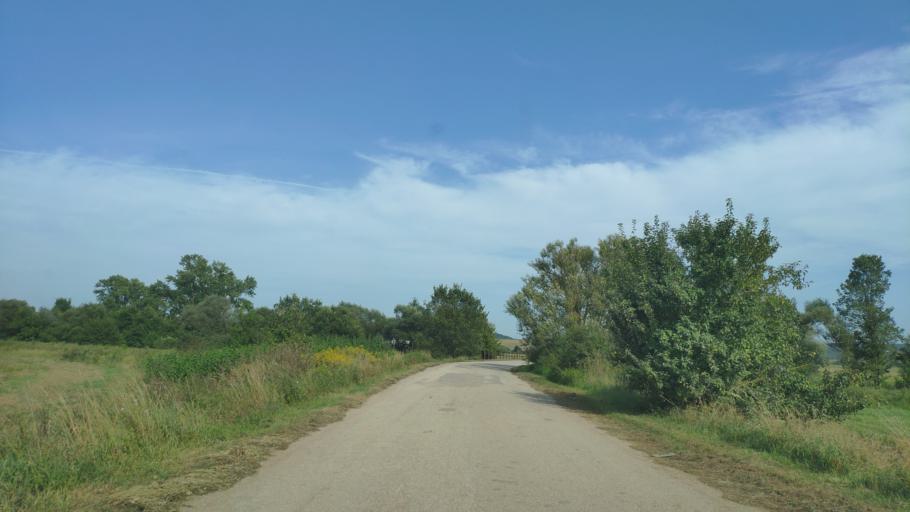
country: HU
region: Borsod-Abauj-Zemplen
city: Putnok
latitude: 48.4541
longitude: 20.3315
